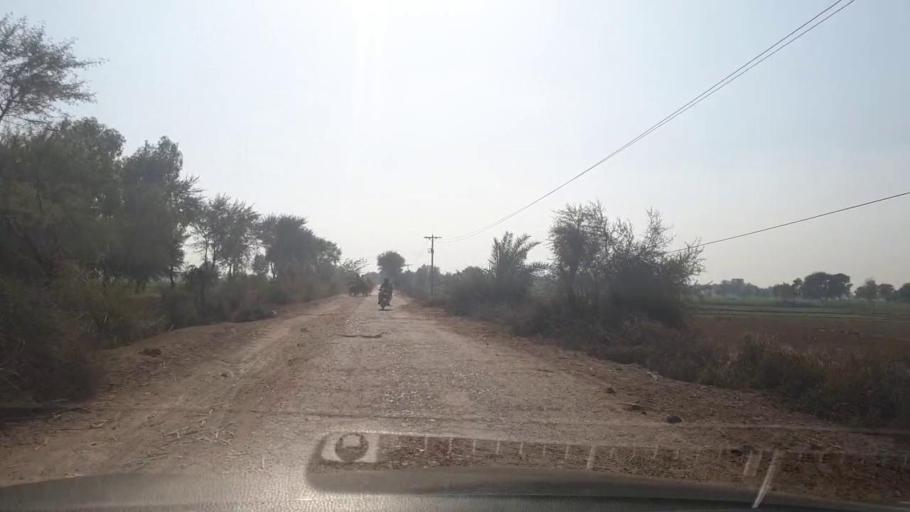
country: PK
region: Sindh
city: Ubauro
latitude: 28.1411
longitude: 69.6500
